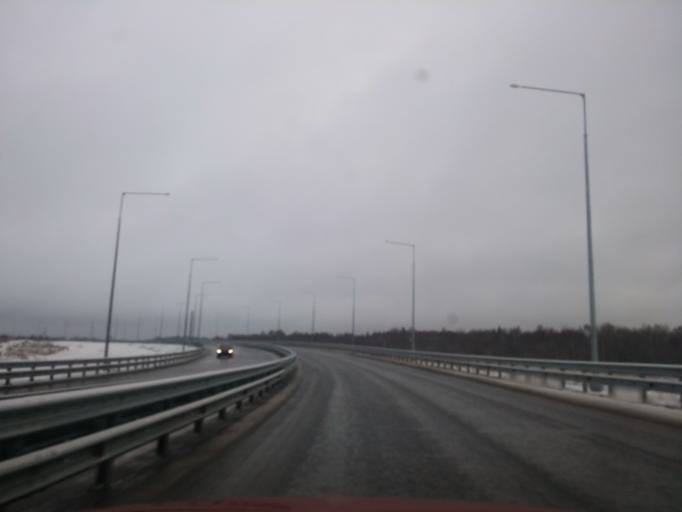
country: RU
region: Tverskaya
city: Likhoslavl'
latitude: 56.9595
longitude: 35.4836
